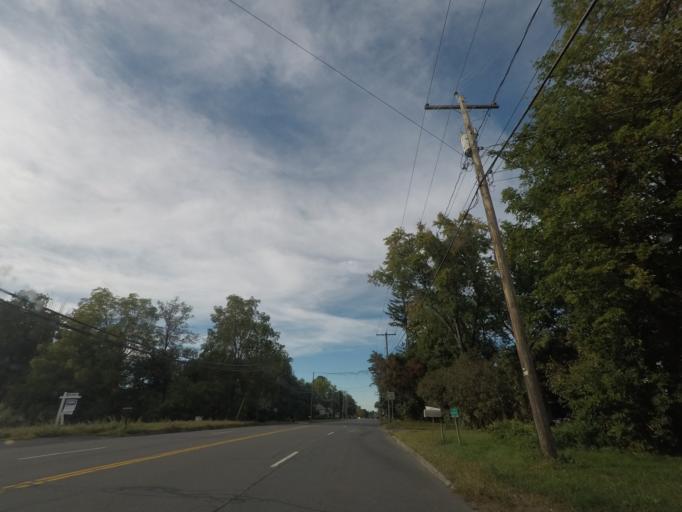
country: US
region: New York
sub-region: Rensselaer County
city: East Greenbush
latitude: 42.5744
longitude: -73.6887
